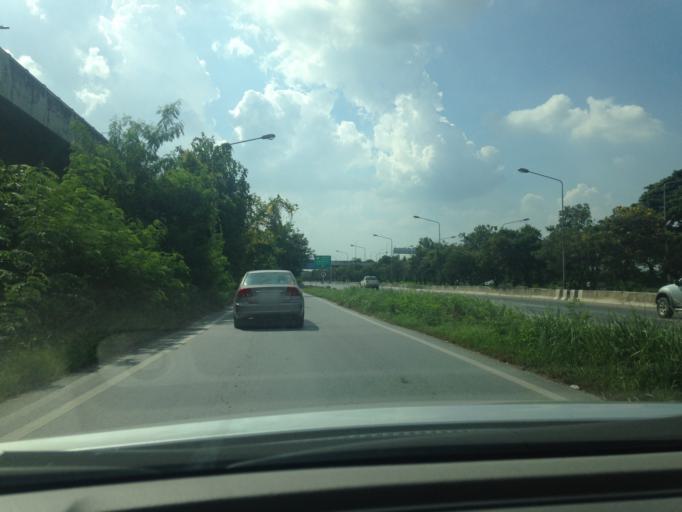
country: TH
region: Pathum Thani
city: Khlong Luang
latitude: 14.0657
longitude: 100.5867
